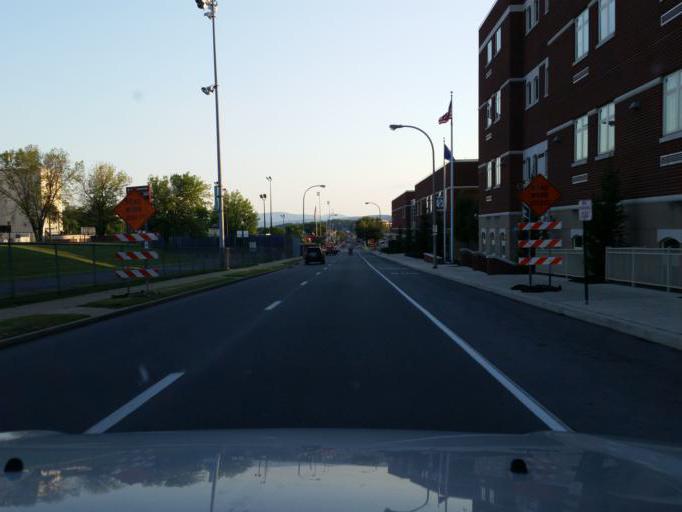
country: US
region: Pennsylvania
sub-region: Blair County
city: Altoona
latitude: 40.5116
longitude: -78.3984
